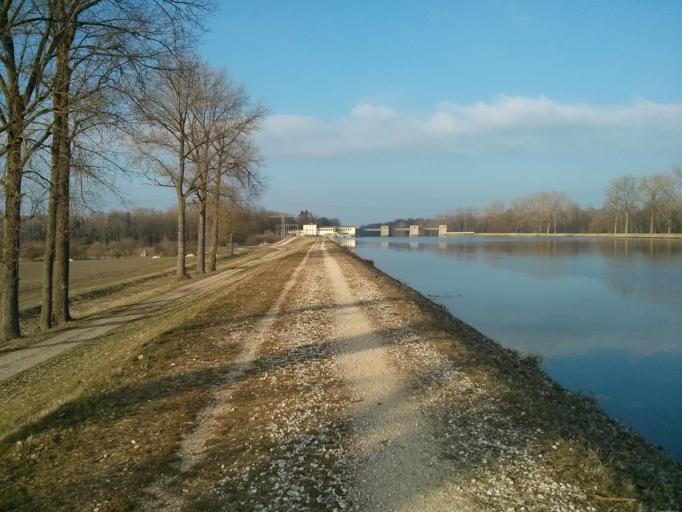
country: DE
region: Bavaria
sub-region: Swabia
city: Ellgau
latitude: 48.5927
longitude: 10.8769
